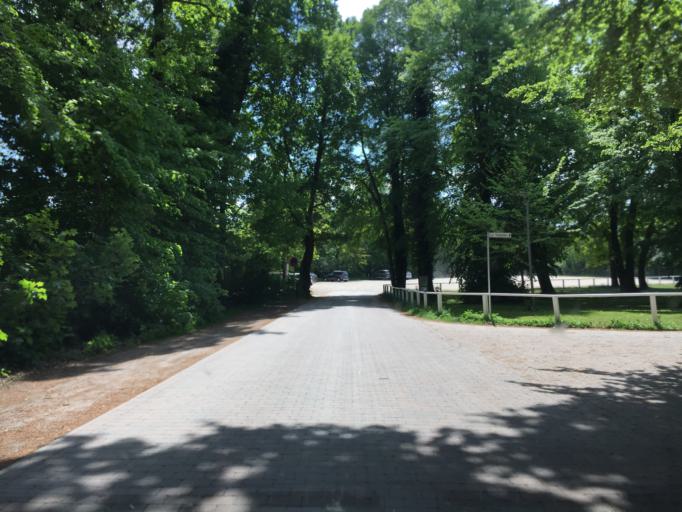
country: DE
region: Lower Saxony
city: Rastede
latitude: 53.2473
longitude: 8.2065
